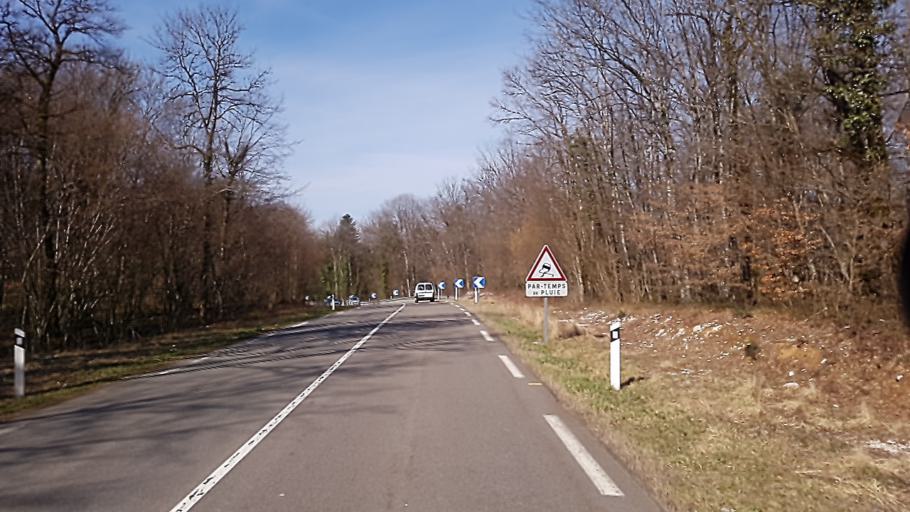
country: FR
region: Franche-Comte
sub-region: Departement du Jura
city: Poligny
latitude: 46.8166
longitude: 5.7735
